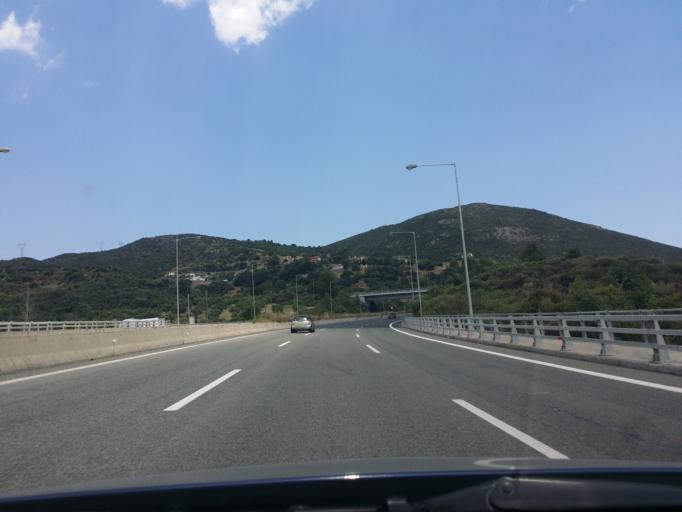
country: GR
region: Peloponnese
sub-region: Nomos Arkadias
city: Megalopoli
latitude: 37.3944
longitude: 22.1791
